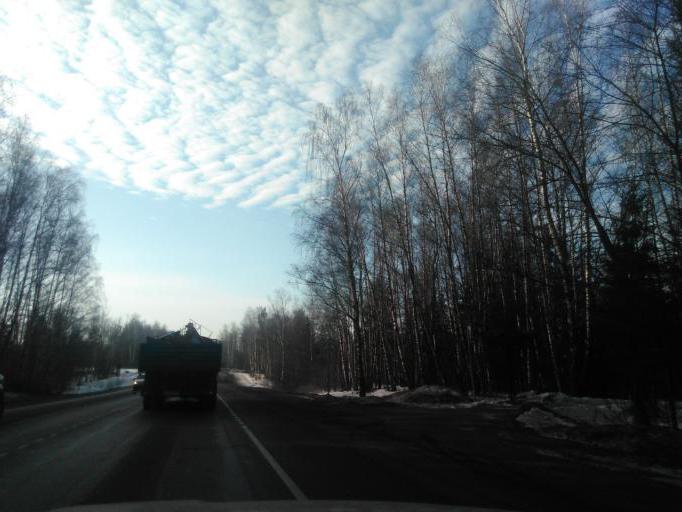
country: RU
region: Moskovskaya
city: Snegiri
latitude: 55.8899
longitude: 36.9442
